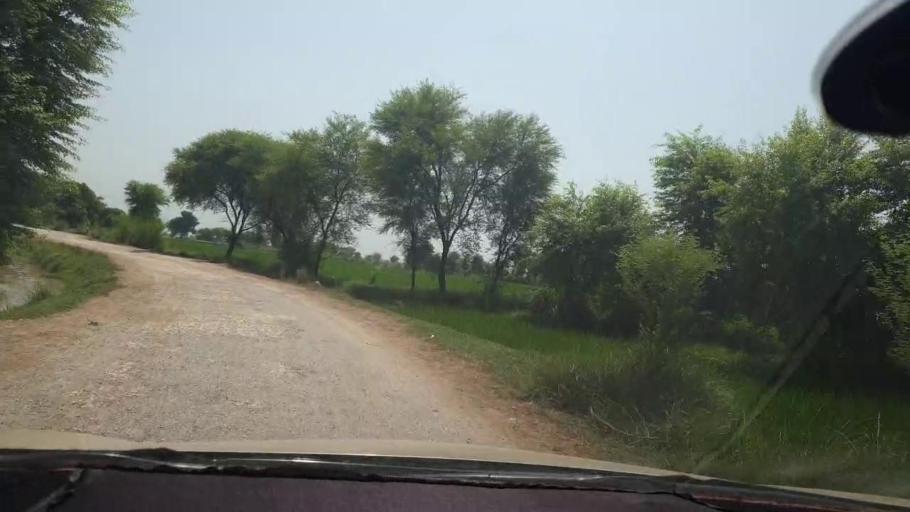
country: PK
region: Sindh
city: Kambar
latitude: 27.6665
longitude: 67.9436
